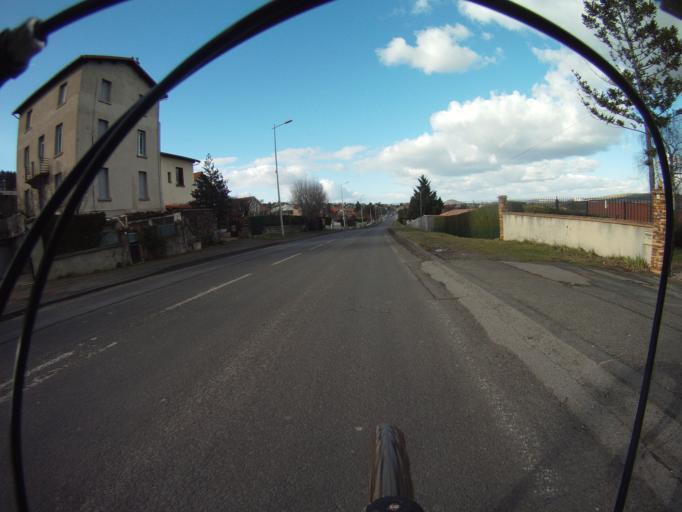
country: FR
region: Auvergne
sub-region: Departement du Puy-de-Dome
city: Perignat-les-Sarlieve
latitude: 45.7317
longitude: 3.1433
